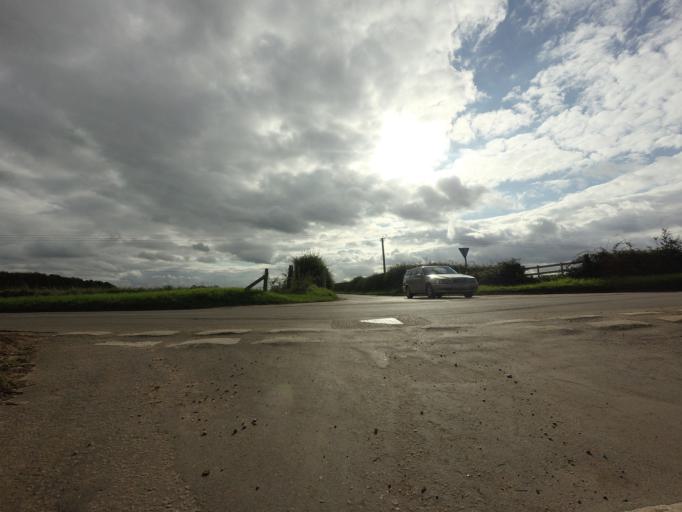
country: GB
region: England
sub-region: Norfolk
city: Snettisham
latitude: 52.8764
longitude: 0.5146
